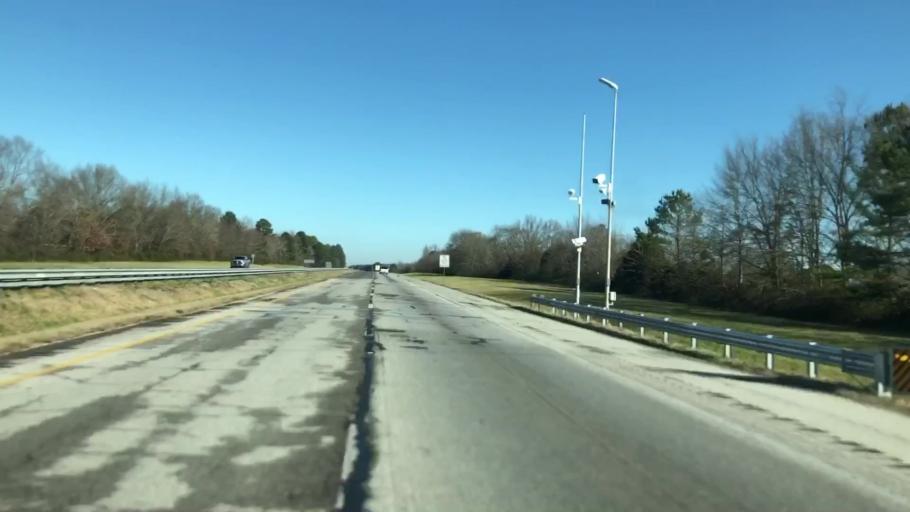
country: US
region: Alabama
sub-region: Limestone County
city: Athens
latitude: 34.8441
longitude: -86.9331
